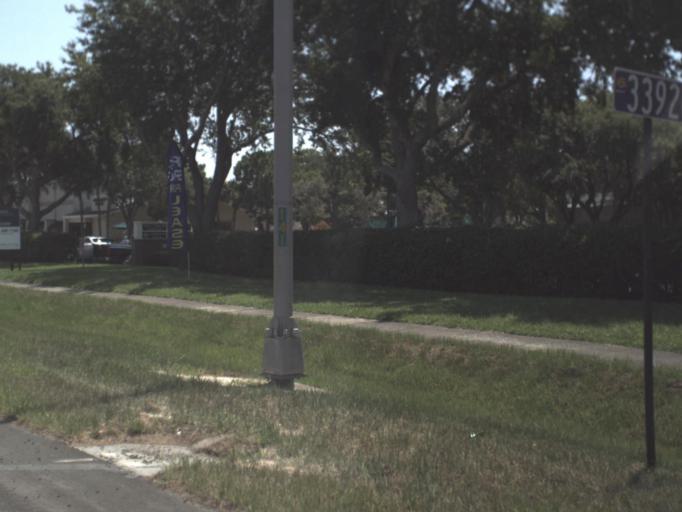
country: US
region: Florida
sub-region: Pinellas County
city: Palm Harbor
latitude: 28.0804
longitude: -82.7394
